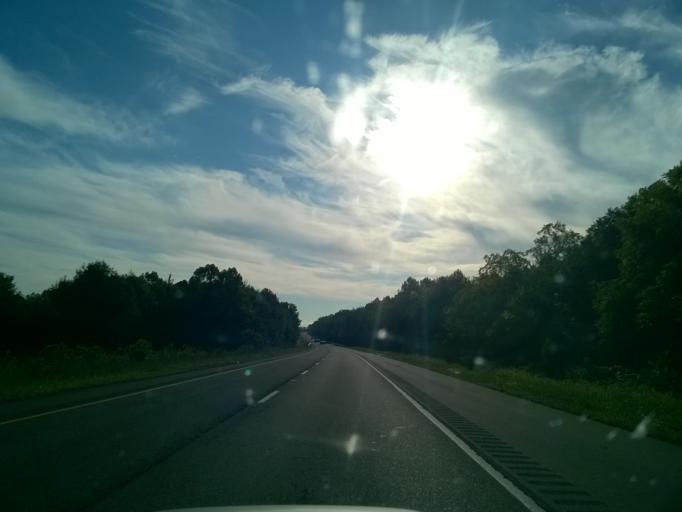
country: US
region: Indiana
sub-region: Warrick County
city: Boonville
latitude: 38.1981
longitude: -87.1723
